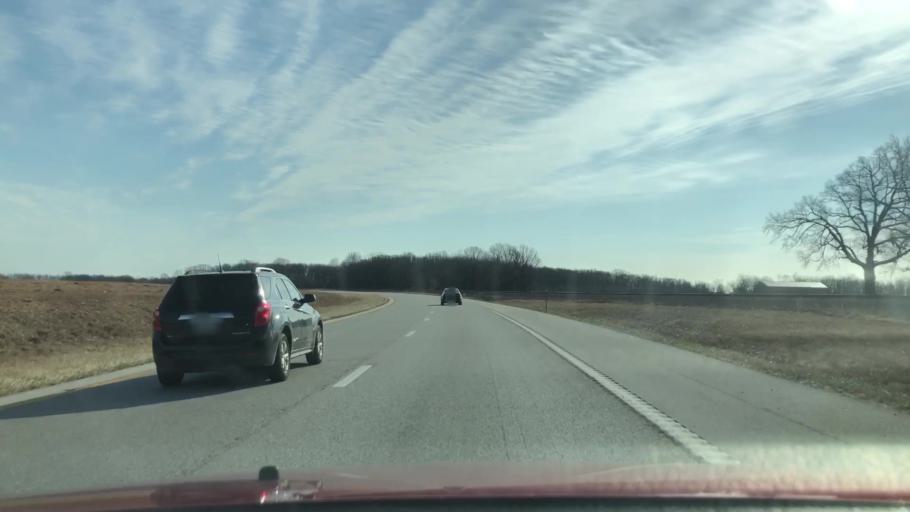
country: US
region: Missouri
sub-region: Webster County
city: Seymour
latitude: 37.1315
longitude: -92.7403
